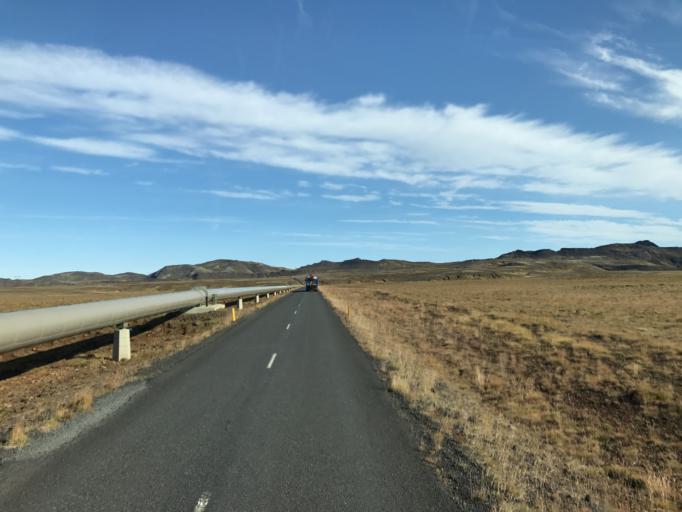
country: IS
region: South
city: Hveragerdi
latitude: 64.1227
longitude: -21.3665
